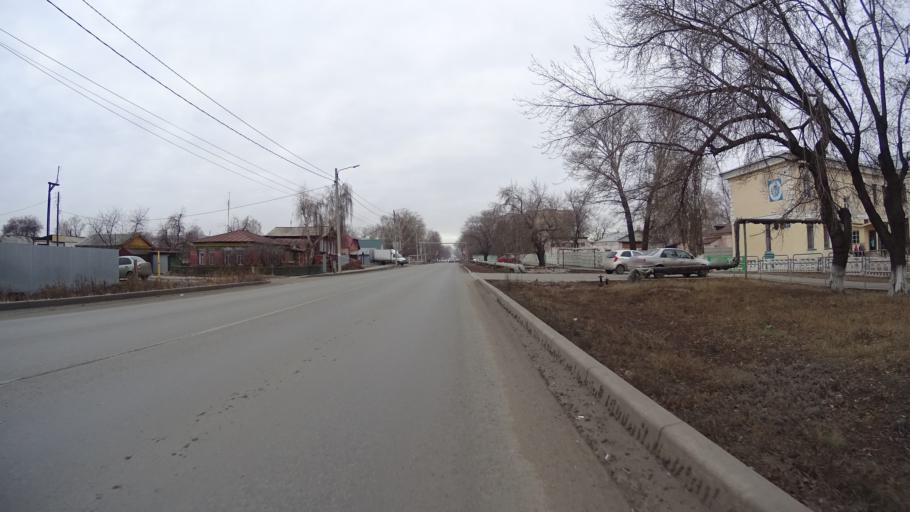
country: RU
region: Chelyabinsk
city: Troitsk
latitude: 54.1100
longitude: 61.5701
